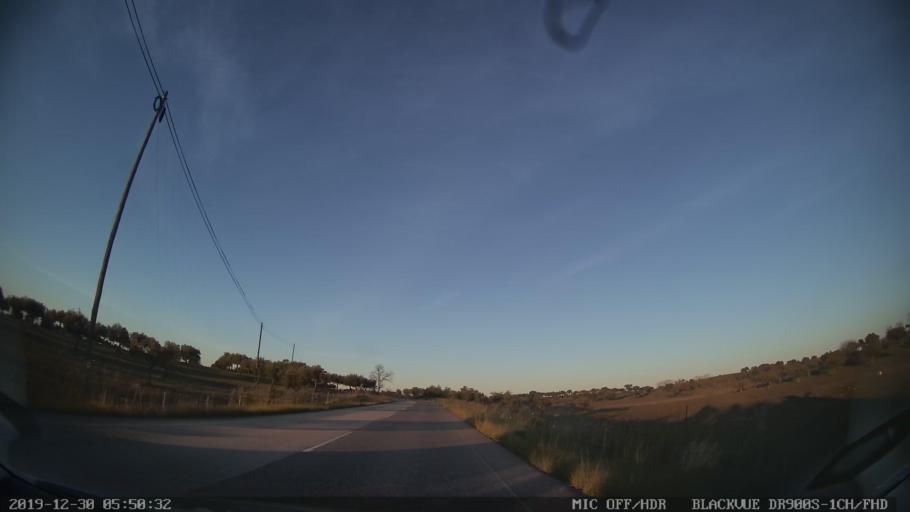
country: PT
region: Castelo Branco
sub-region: Idanha-A-Nova
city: Idanha-a-Nova
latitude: 39.9851
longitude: -7.2422
